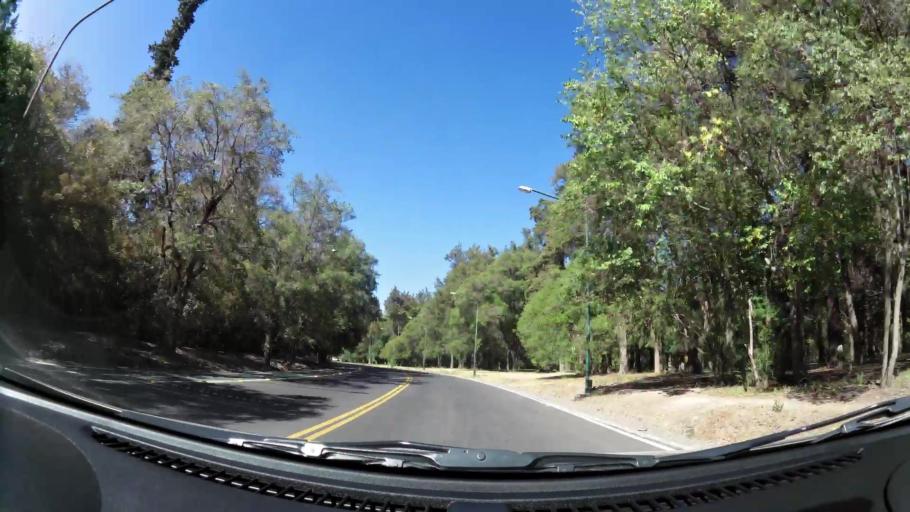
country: AR
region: Mendoza
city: Mendoza
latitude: -32.8898
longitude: -68.8728
